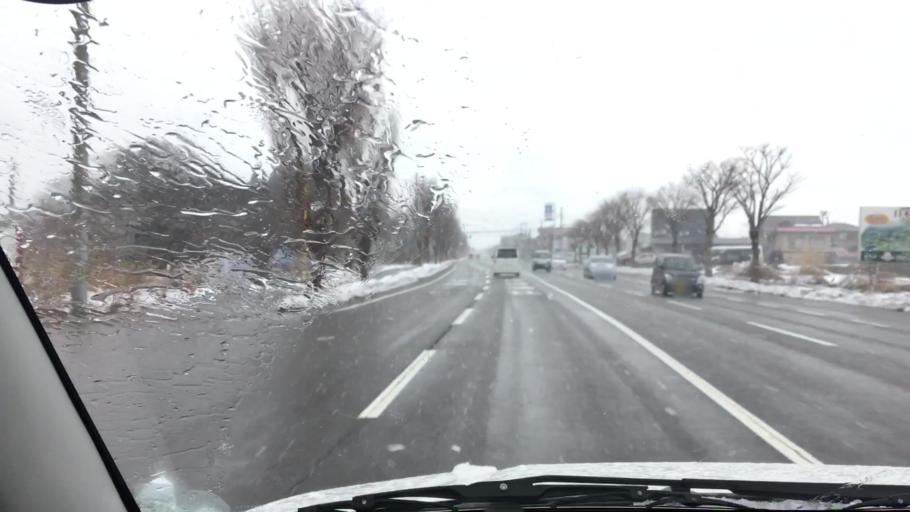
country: JP
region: Niigata
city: Joetsu
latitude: 37.1158
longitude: 138.2330
